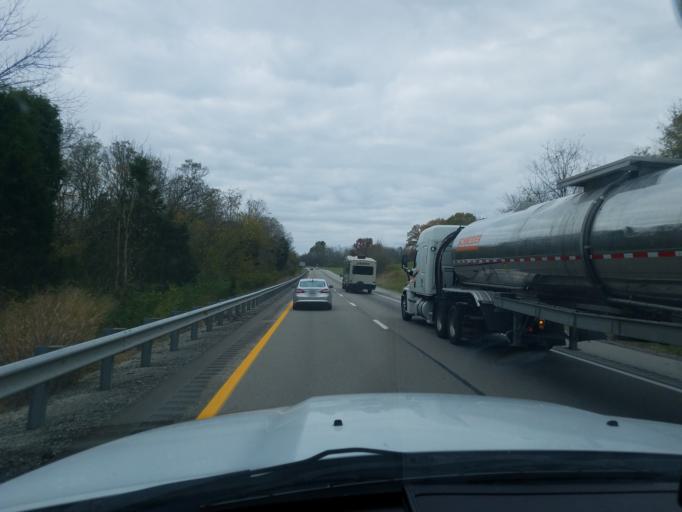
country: US
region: Indiana
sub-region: Switzerland County
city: Vevay
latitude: 38.6758
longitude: -85.0034
